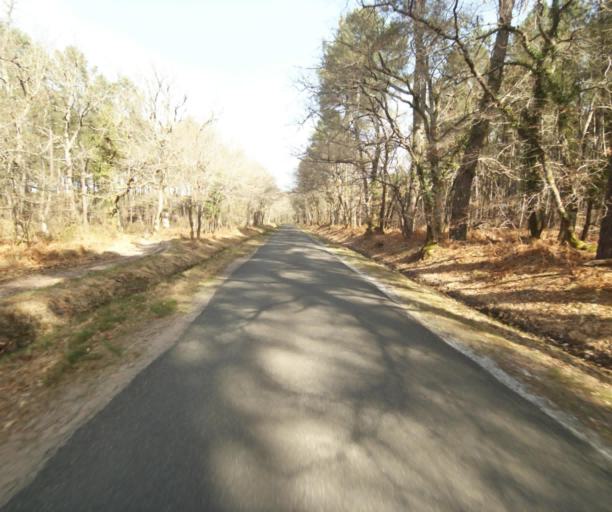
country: FR
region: Aquitaine
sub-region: Departement de la Gironde
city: Bazas
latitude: 44.2357
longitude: -0.2013
